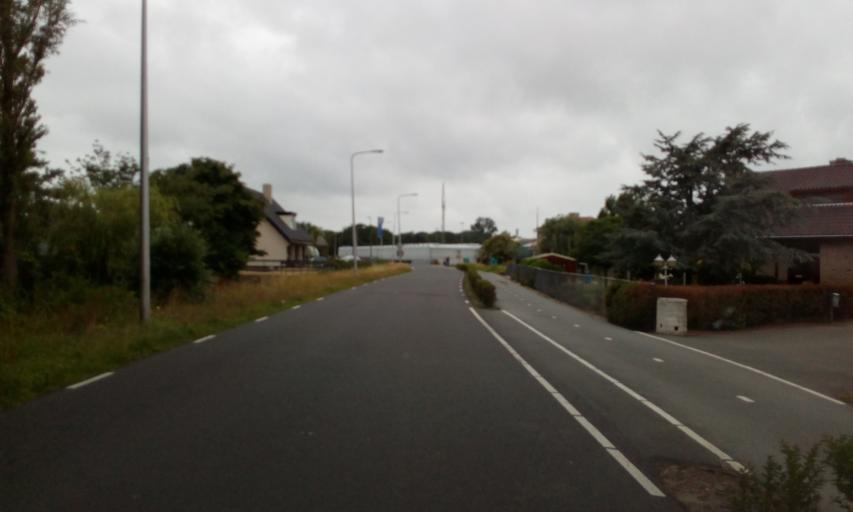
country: NL
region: South Holland
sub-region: Gemeente Westland
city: Monster
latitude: 52.0317
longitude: 4.1920
